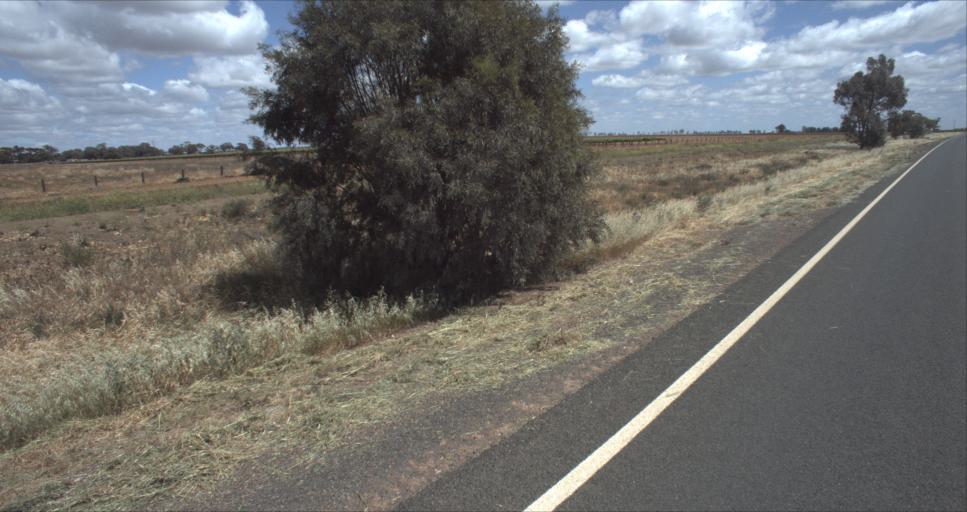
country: AU
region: New South Wales
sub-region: Murrumbidgee Shire
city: Darlington Point
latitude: -34.4787
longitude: 146.1520
